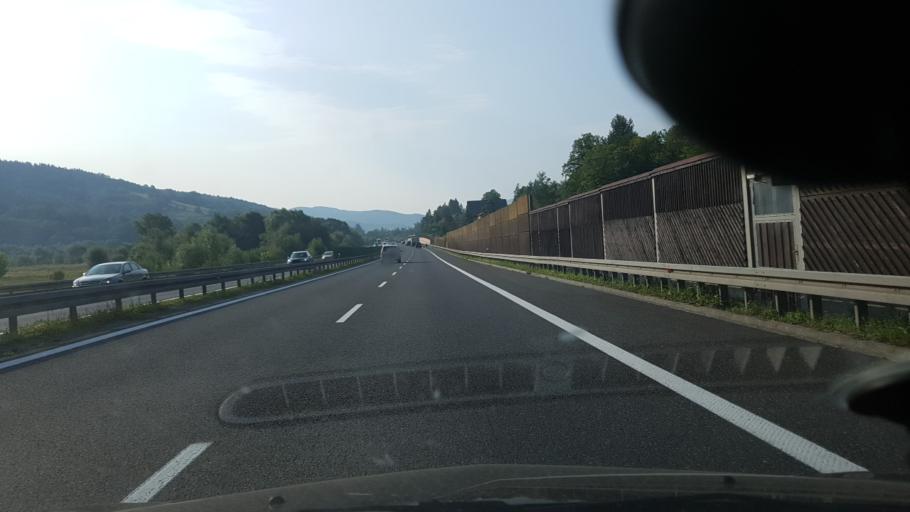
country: PL
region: Lesser Poland Voivodeship
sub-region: Powiat myslenicki
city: Stroza
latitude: 49.7817
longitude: 19.9519
